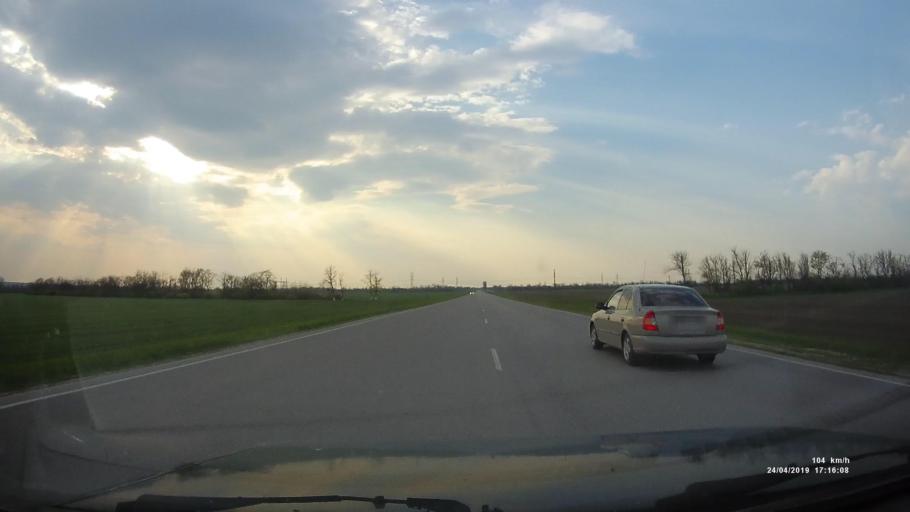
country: RU
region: Rostov
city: Gigant
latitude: 46.4959
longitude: 41.4312
